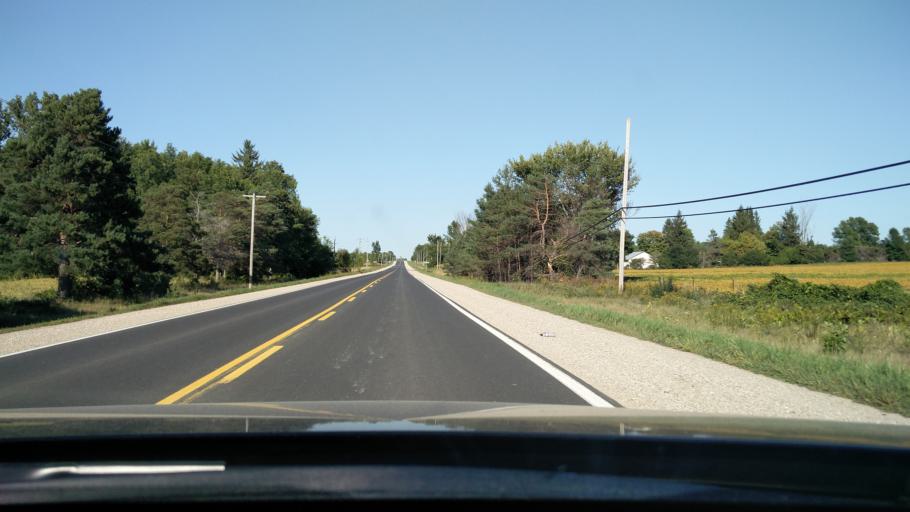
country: CA
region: Ontario
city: Perth
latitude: 44.8559
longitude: -76.2978
